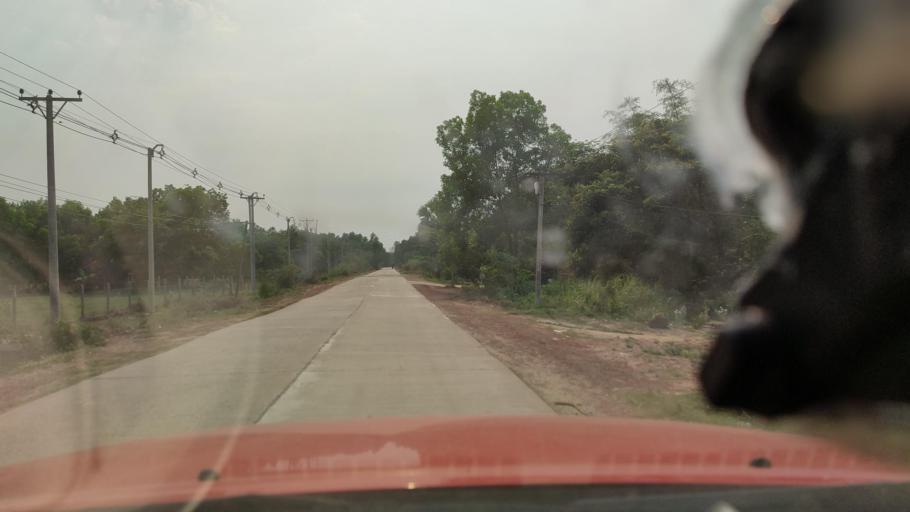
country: MM
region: Ayeyarwady
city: Nyaungdon
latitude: 17.1612
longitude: 95.9223
